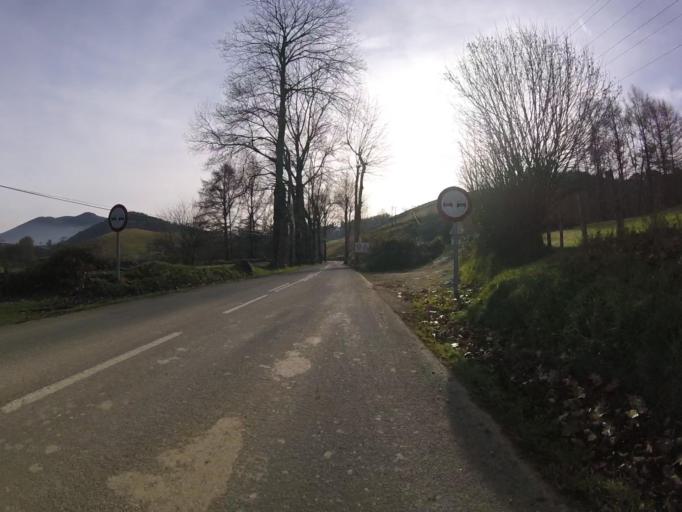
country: ES
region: Basque Country
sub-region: Provincia de Guipuzcoa
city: Berastegui
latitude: 43.1072
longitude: -1.9633
